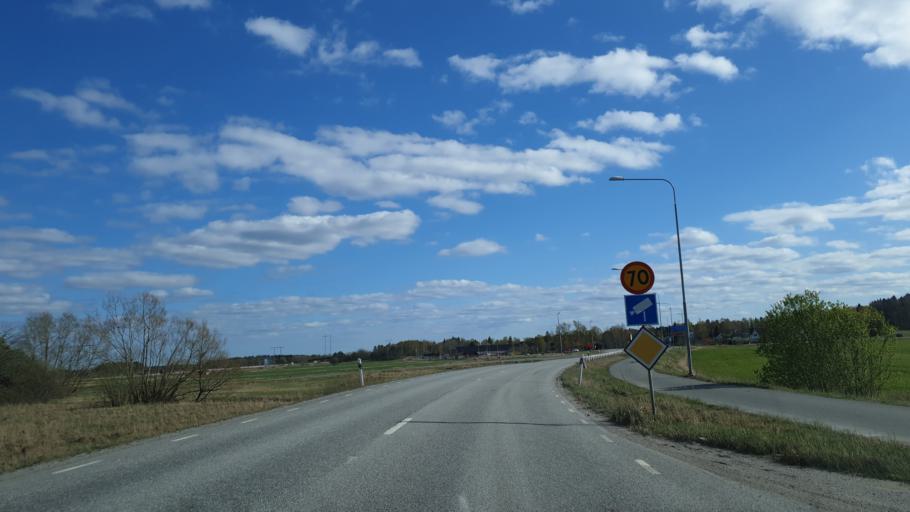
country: SE
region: Stockholm
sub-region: Sigtuna Kommun
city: Rosersberg
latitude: 59.5925
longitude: 17.8906
